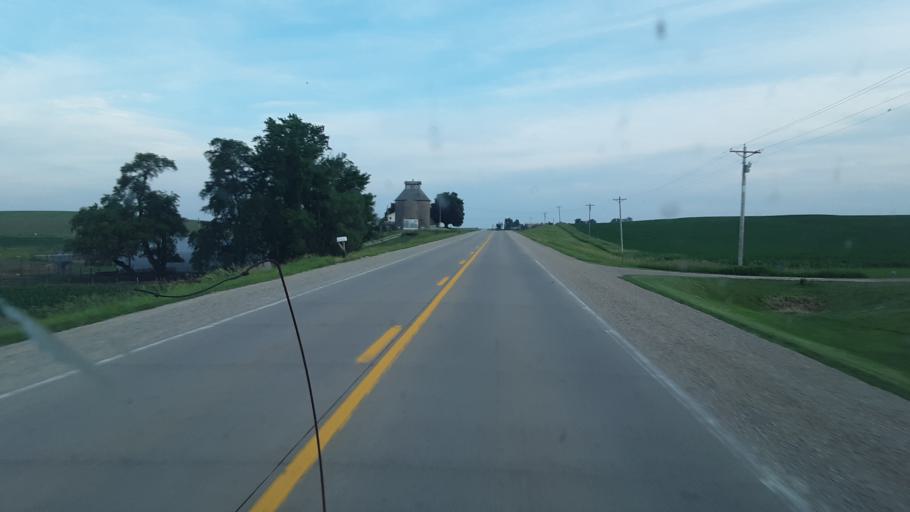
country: US
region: Iowa
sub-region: Benton County
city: Belle Plaine
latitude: 41.7797
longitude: -92.2793
